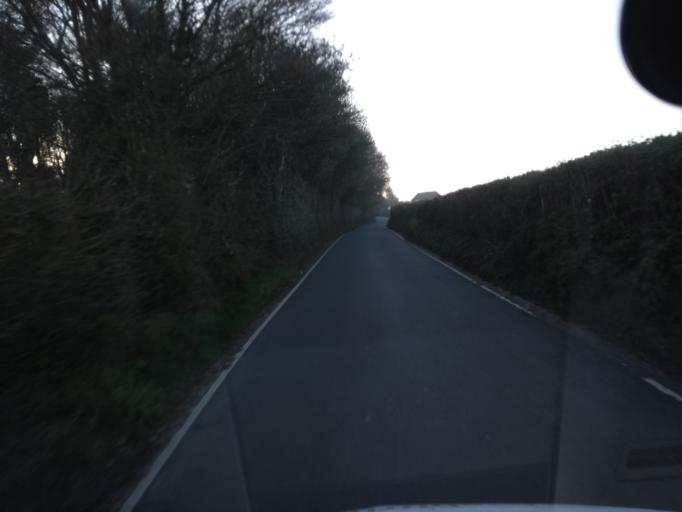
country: GB
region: England
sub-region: Somerset
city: Crewkerne
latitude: 50.8405
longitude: -2.8753
